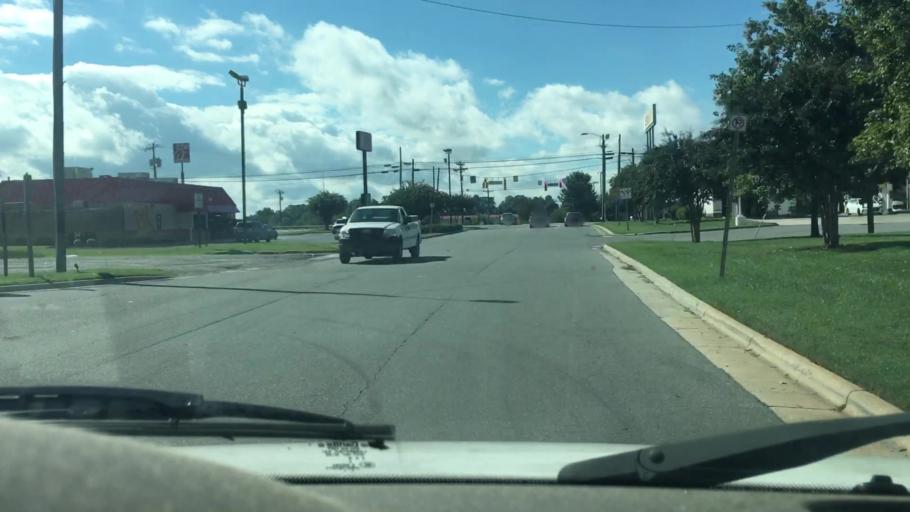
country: US
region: North Carolina
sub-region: Iredell County
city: Mooresville
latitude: 35.5955
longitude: -80.8627
